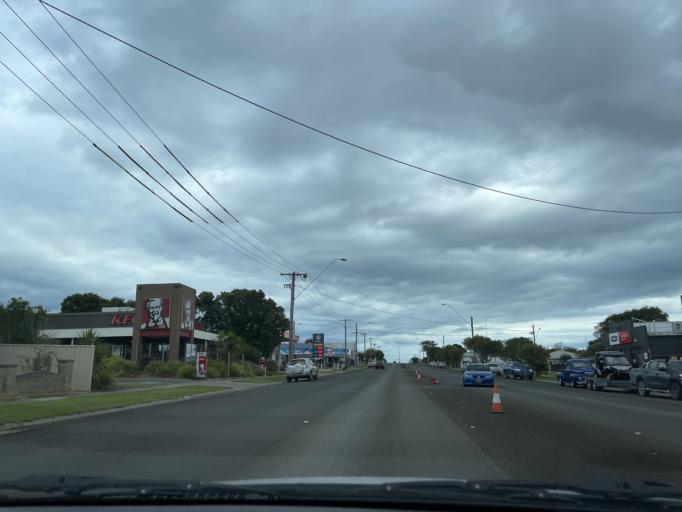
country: AU
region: Victoria
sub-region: Glenelg
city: Portland
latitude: -38.3369
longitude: 141.6042
